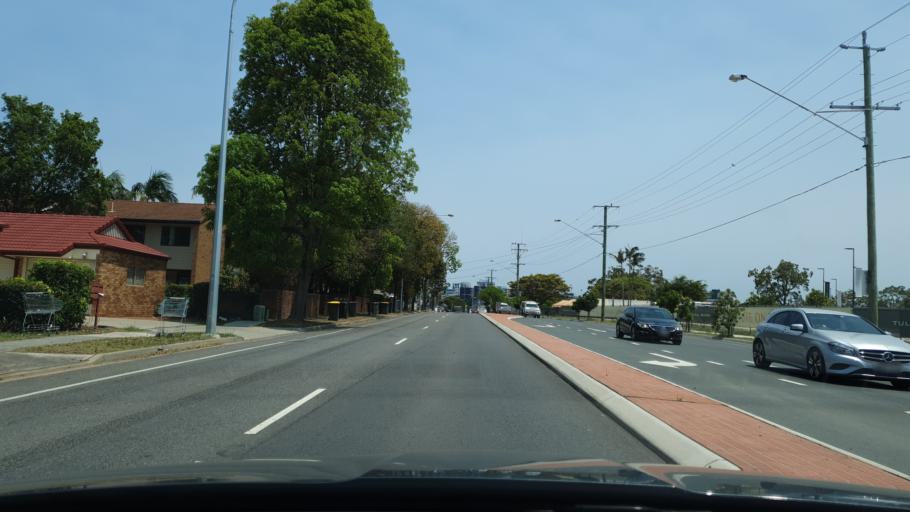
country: AU
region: Queensland
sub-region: Brisbane
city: Ascot
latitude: -27.4287
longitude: 153.0722
